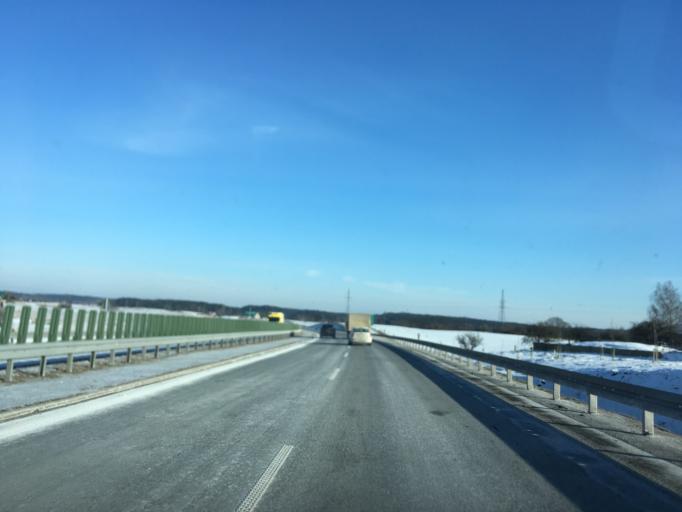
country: PL
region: Pomeranian Voivodeship
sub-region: Powiat koscierski
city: Koscierzyna
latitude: 54.1076
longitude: 17.9635
